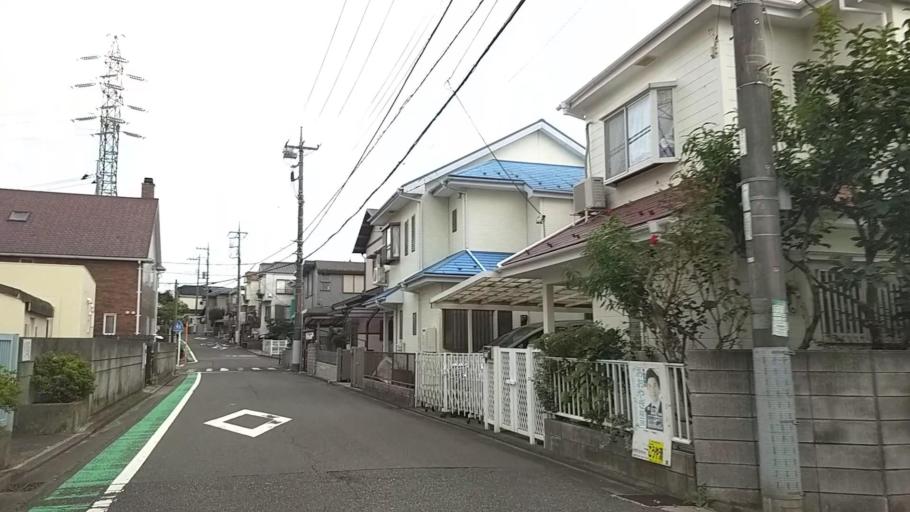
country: JP
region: Kanagawa
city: Yokohama
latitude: 35.4836
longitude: 139.5659
